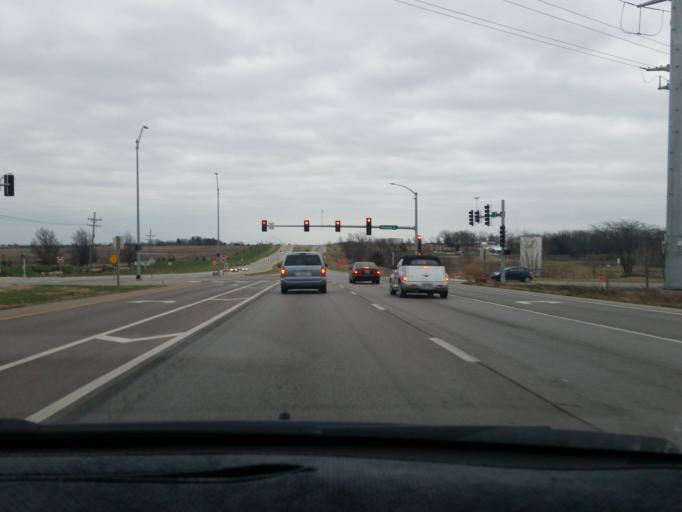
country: US
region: Kansas
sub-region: Douglas County
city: Lawrence
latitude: 38.9426
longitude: -95.2058
